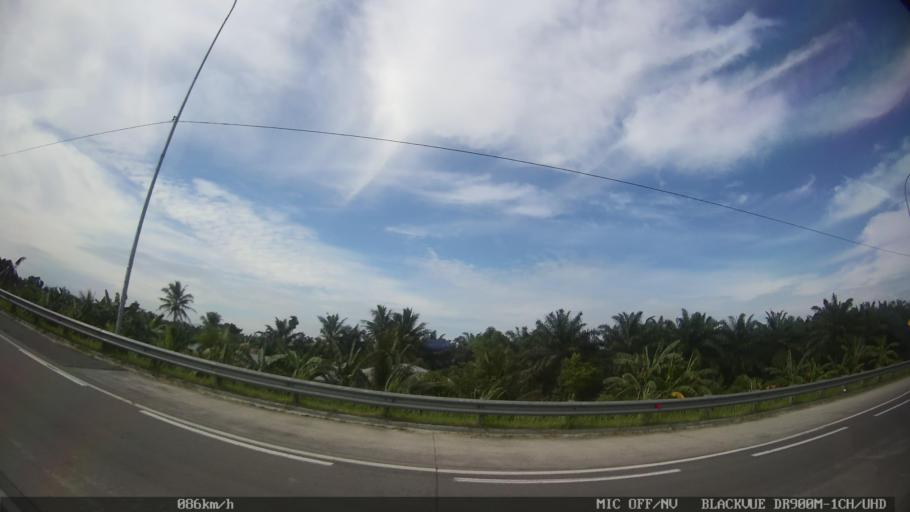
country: ID
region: North Sumatra
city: Binjai
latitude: 3.6462
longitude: 98.5503
